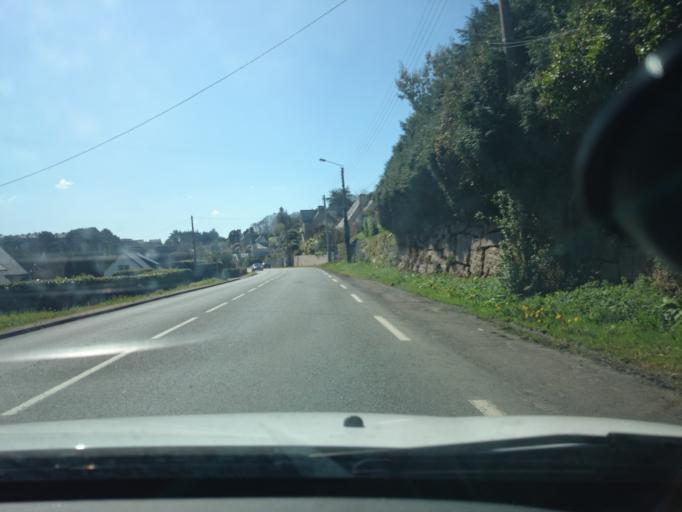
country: FR
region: Brittany
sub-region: Departement des Cotes-d'Armor
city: Perros-Guirec
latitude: 48.8128
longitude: -3.4636
